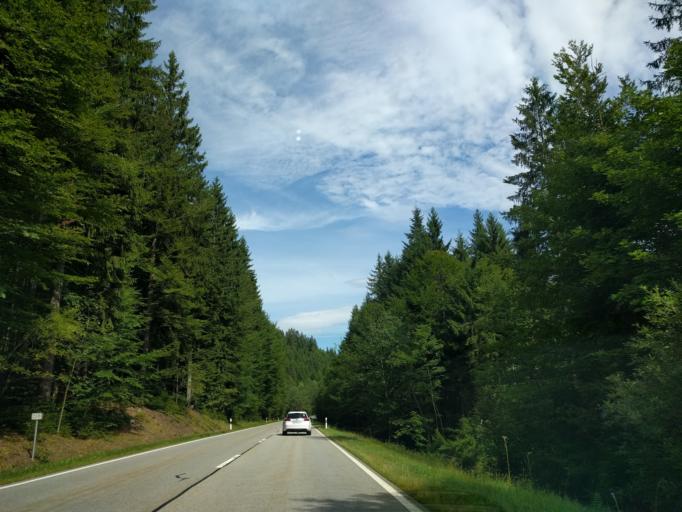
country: DE
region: Bavaria
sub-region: Lower Bavaria
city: Bodenmais
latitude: 49.0395
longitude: 13.1171
